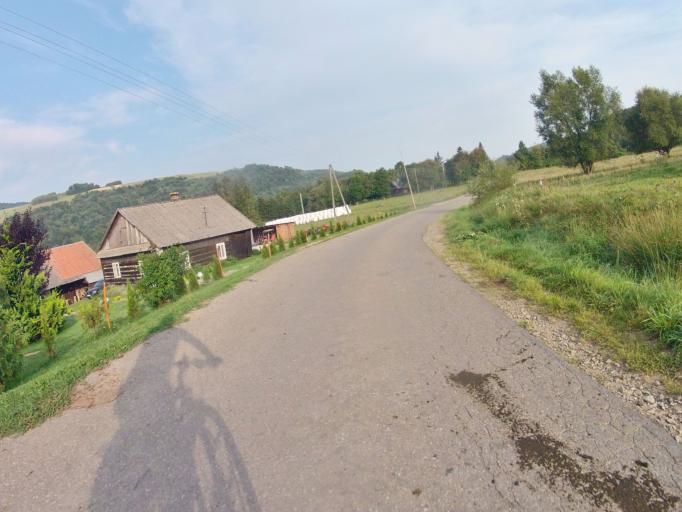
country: PL
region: Subcarpathian Voivodeship
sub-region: Powiat jasielski
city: Krempna
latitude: 49.5470
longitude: 21.5482
